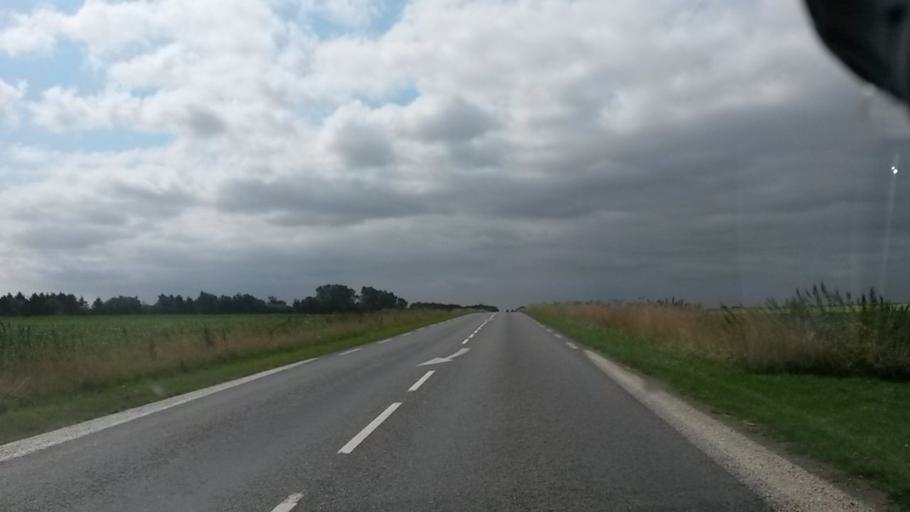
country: FR
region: Nord-Pas-de-Calais
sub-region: Departement du Pas-de-Calais
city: Vaulx-Vraucourt
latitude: 50.1180
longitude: 2.9250
